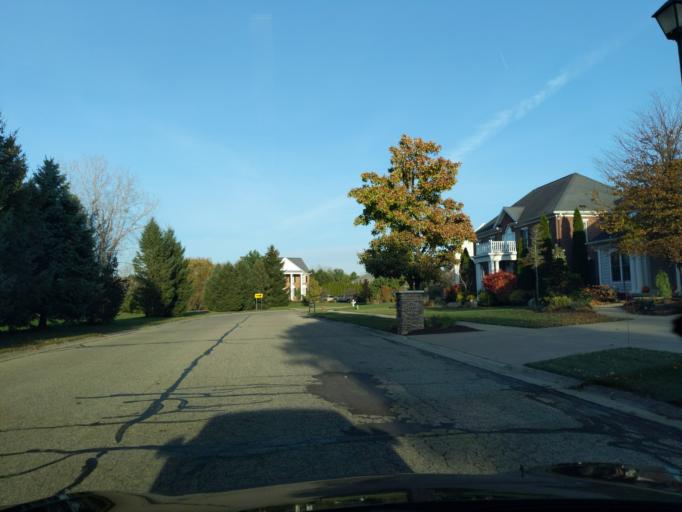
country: US
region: Michigan
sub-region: Clinton County
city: Bath
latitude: 42.7996
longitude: -84.4689
